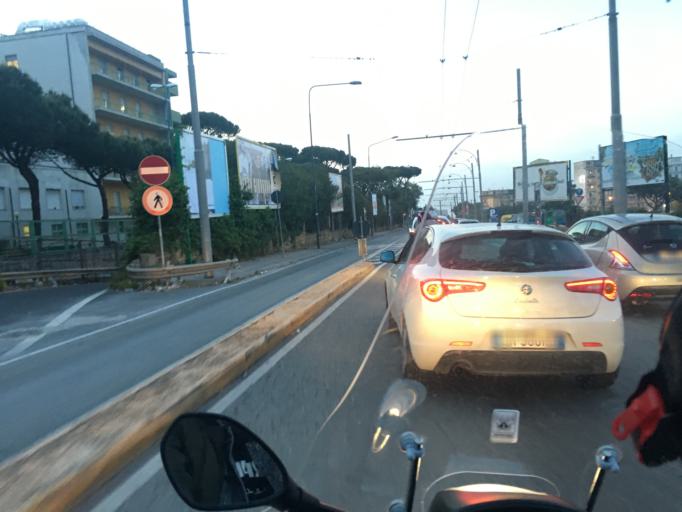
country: IT
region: Campania
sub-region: Provincia di Napoli
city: Napoli
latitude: 40.8665
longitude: 14.2271
